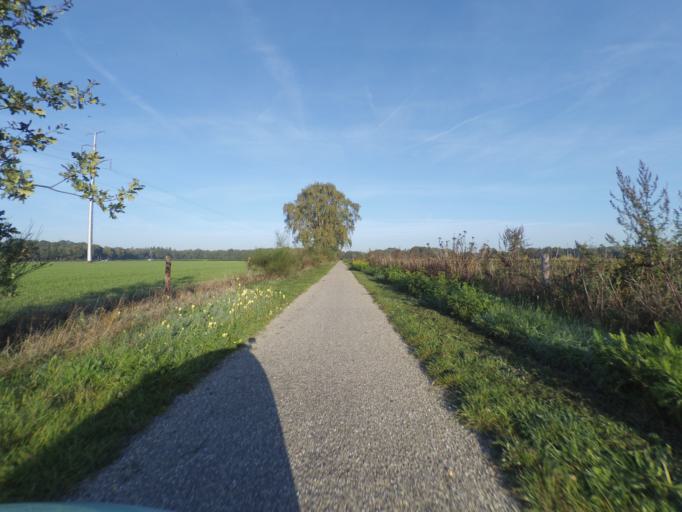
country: NL
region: Gelderland
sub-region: Gemeente Winterswijk
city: Winterswijk
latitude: 51.9799
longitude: 6.6938
